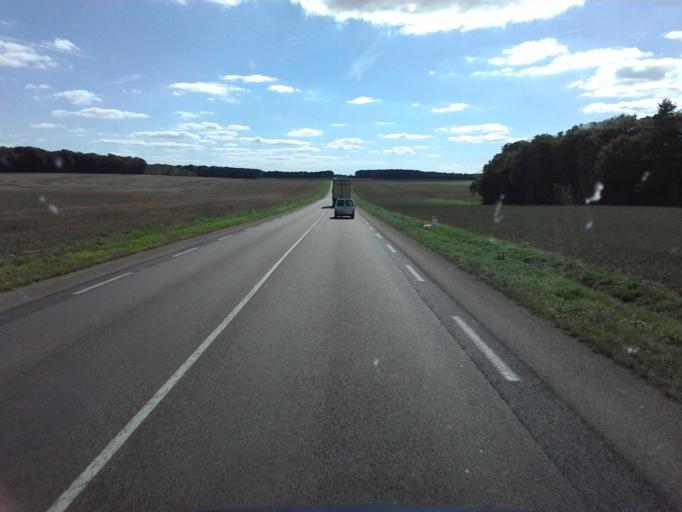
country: FR
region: Bourgogne
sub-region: Departement de la Cote-d'Or
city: Chatillon-sur-Seine
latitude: 47.7839
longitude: 4.5105
